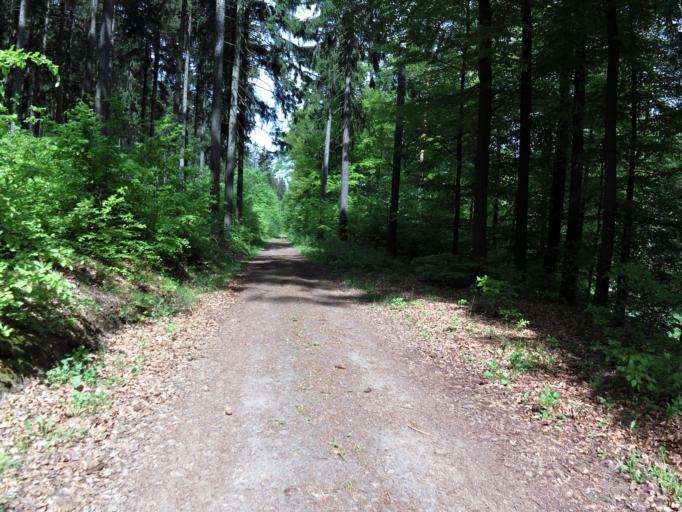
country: DE
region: Thuringia
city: Georgenthal
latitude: 50.8232
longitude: 10.6664
